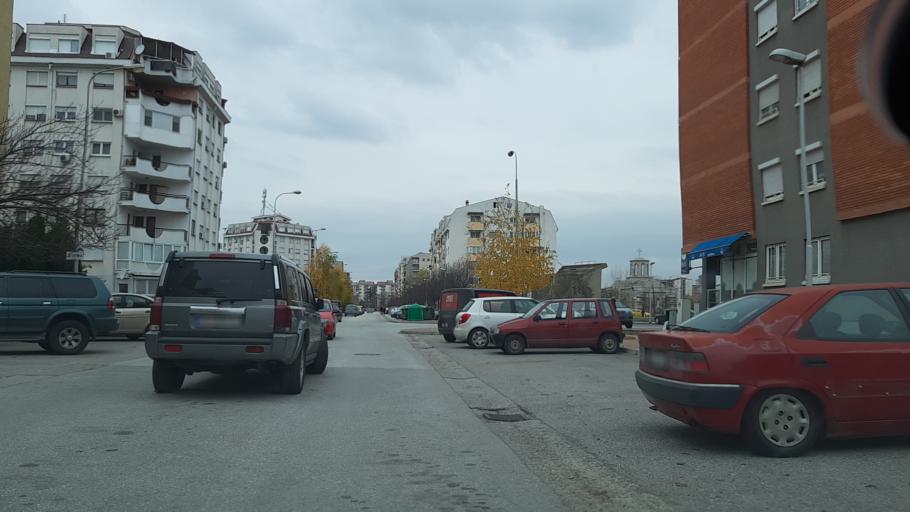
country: MK
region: Kisela Voda
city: Usje
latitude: 41.9790
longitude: 21.4756
